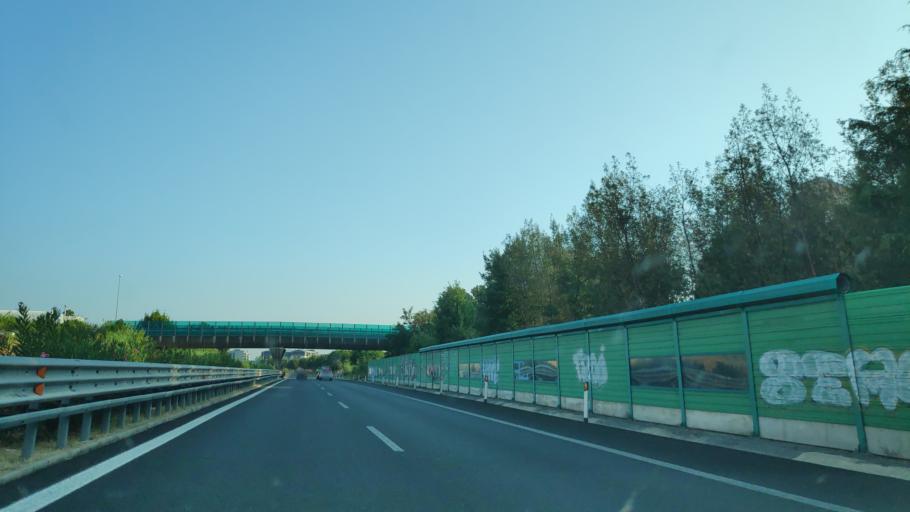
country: IT
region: Calabria
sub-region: Provincia di Cosenza
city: Quattromiglia
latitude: 39.3245
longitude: 16.2398
